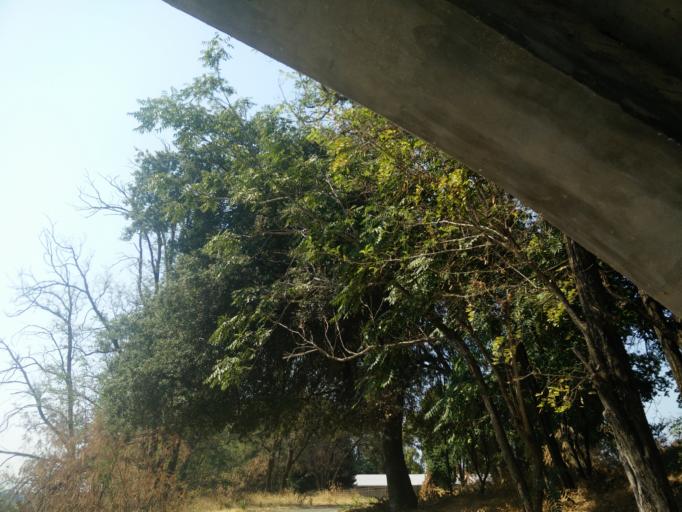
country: US
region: California
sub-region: Shasta County
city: Redding
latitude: 40.5940
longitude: -122.4017
